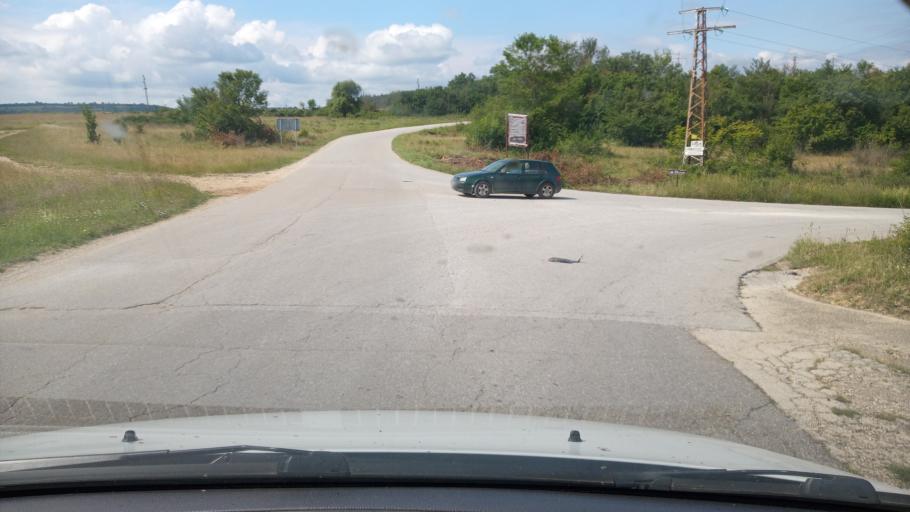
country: BG
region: Pleven
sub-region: Obshtina Cherven Bryag
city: Cherven Bryag
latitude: 43.1795
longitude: 24.0791
